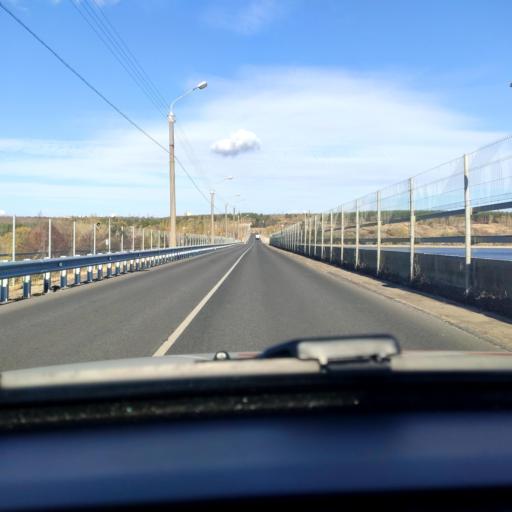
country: RU
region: Voronezj
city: Shilovo
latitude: 51.5463
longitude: 39.1365
